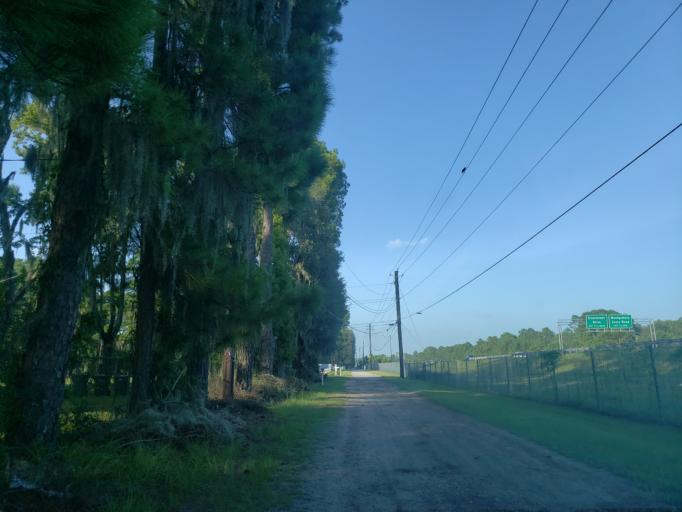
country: US
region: Georgia
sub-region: Chatham County
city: Isle of Hope
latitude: 31.9814
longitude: -81.0916
